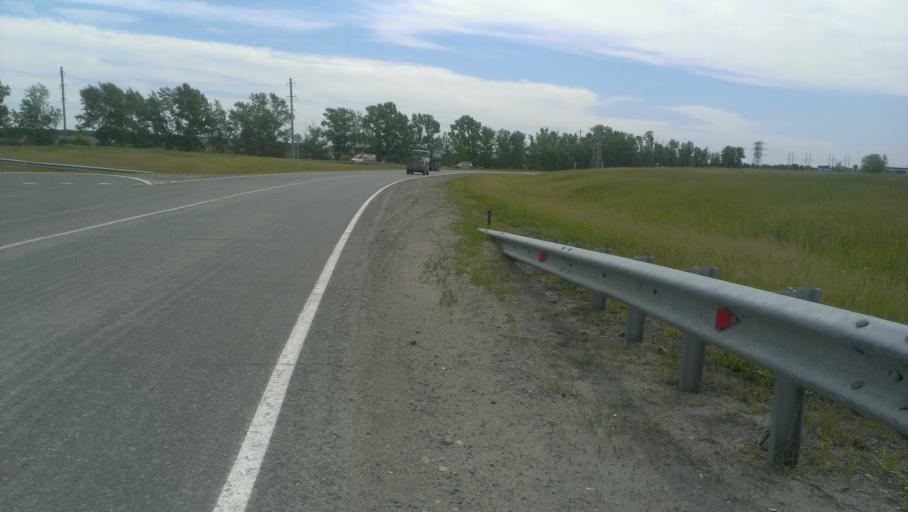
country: RU
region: Altai Krai
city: Sannikovo
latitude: 53.3404
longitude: 83.9369
